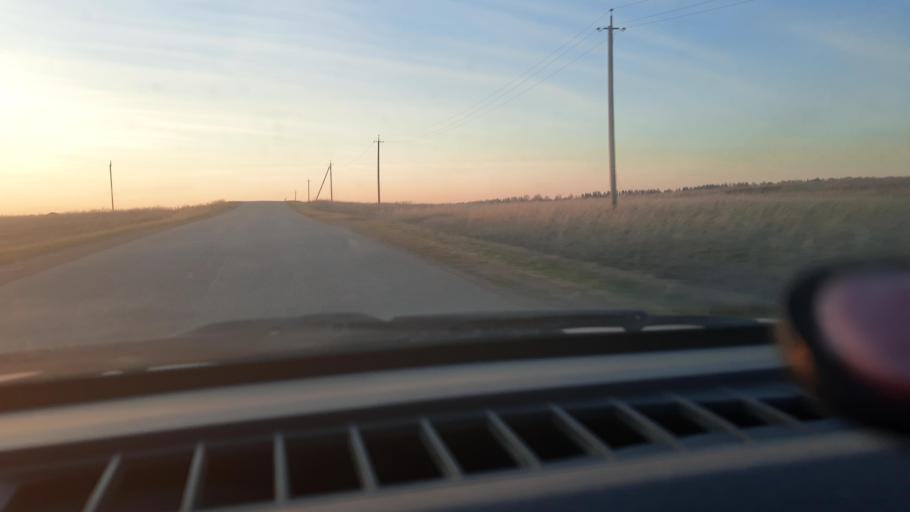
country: RU
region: Bashkortostan
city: Asanovo
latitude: 54.8153
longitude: 55.4792
